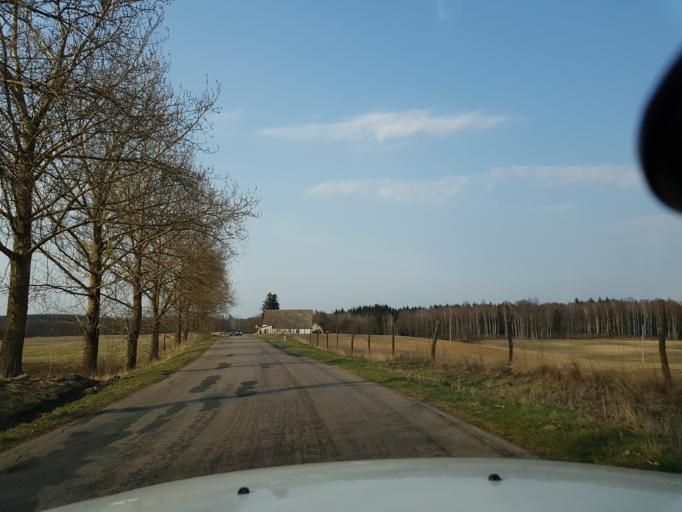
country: PL
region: West Pomeranian Voivodeship
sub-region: Powiat swidwinski
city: Polczyn-Zdroj
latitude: 53.7230
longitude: 16.0715
